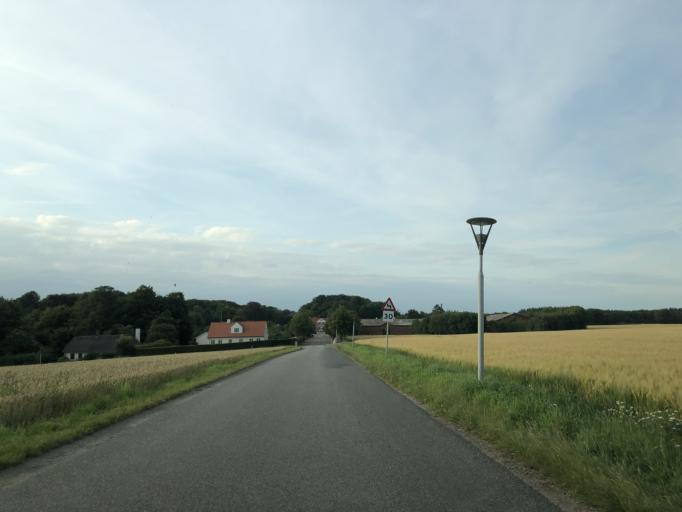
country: DK
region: South Denmark
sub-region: Fredericia Kommune
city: Taulov
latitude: 55.5965
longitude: 9.6048
